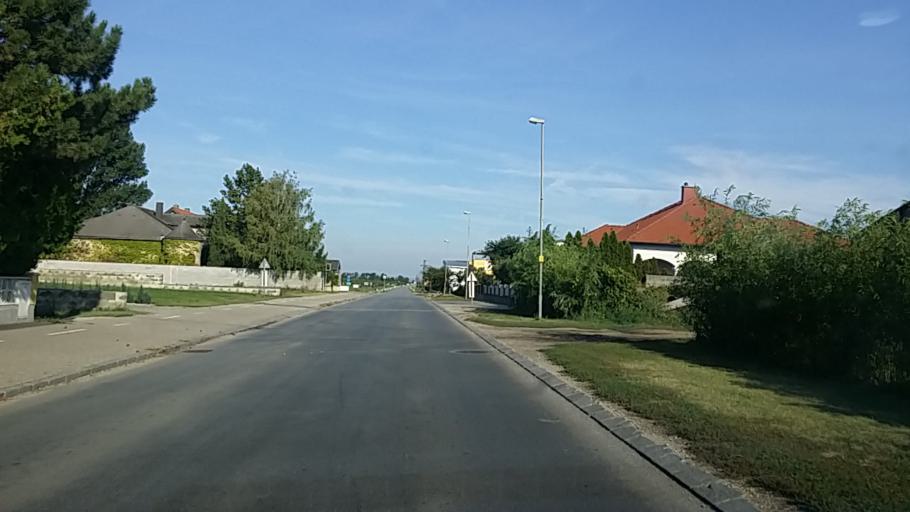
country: AT
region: Burgenland
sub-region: Politischer Bezirk Neusiedl am See
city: Pamhagen
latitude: 47.7041
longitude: 16.9001
